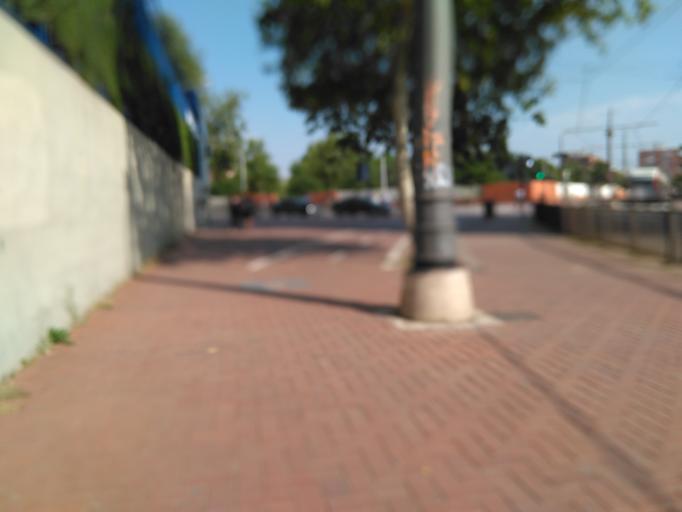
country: ES
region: Valencia
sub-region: Provincia de Valencia
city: Valencia
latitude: 39.4887
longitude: -0.3843
